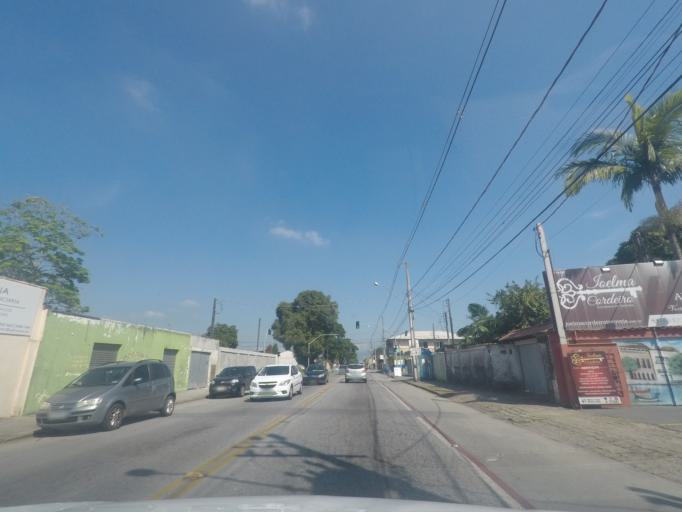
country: BR
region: Parana
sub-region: Paranagua
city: Paranagua
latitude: -25.5330
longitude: -48.5245
